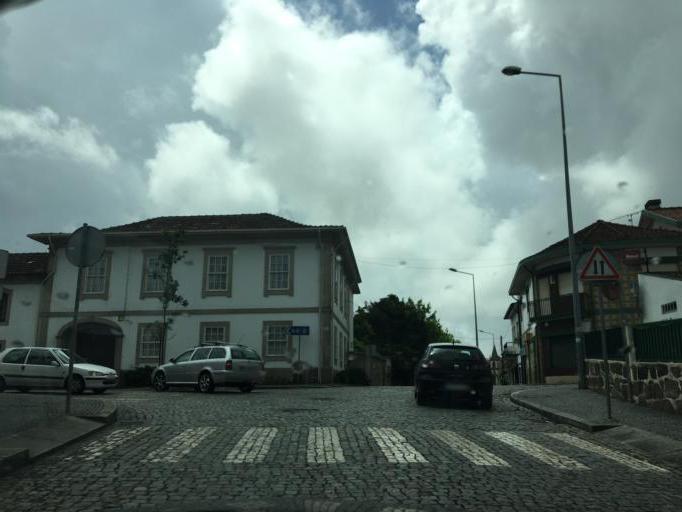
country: PT
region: Porto
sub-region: Maia
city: Nogueira
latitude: 41.2436
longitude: -8.6030
